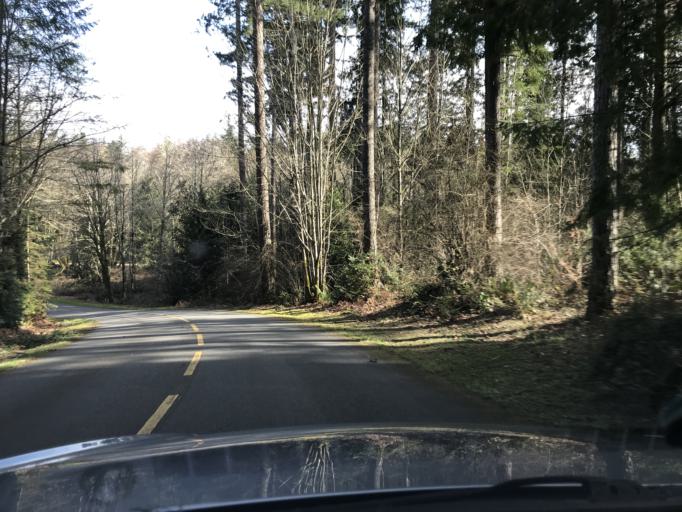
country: US
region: Washington
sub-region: Pierce County
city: Longbranch
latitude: 47.2242
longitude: -122.8045
